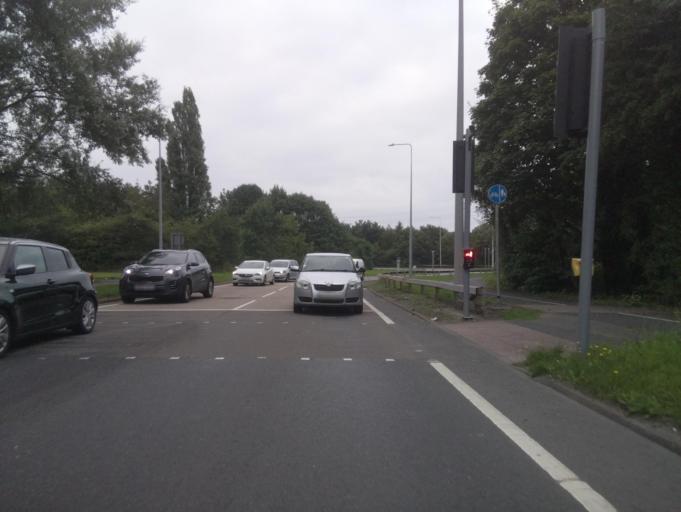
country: GB
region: England
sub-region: Shropshire
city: Hadley
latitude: 52.6950
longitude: -2.4907
